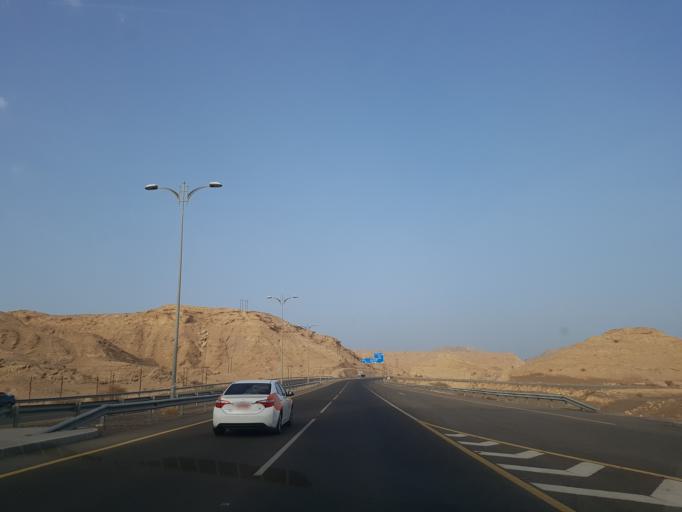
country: OM
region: Al Buraimi
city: Al Buraymi
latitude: 24.2333
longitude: 55.9364
